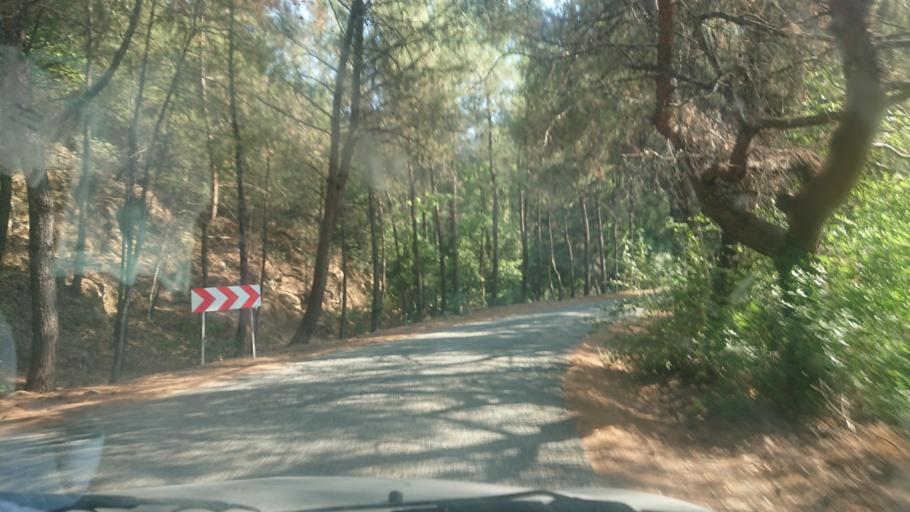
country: TR
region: Aydin
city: Atburgazi
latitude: 37.6912
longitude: 27.1531
